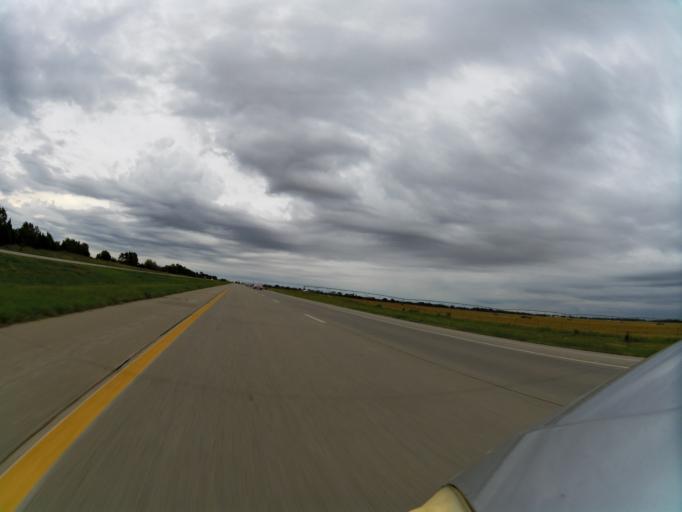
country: US
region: Kansas
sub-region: Reno County
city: South Hutchinson
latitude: 37.9539
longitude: -97.8999
